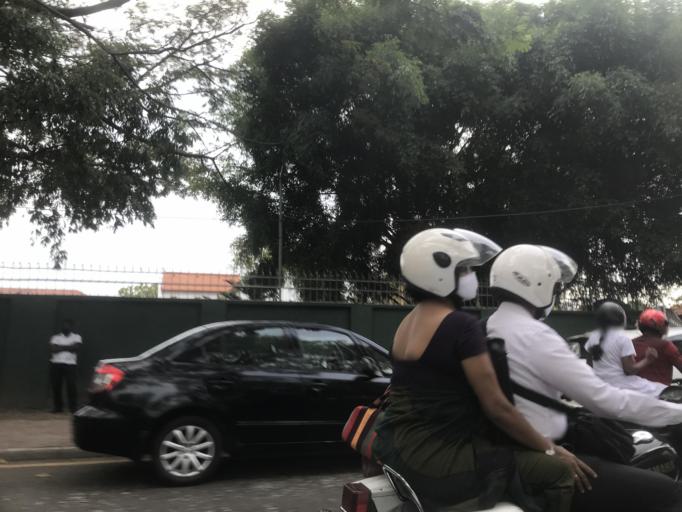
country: LK
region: Western
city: Colombo
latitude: 6.9105
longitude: 79.8640
